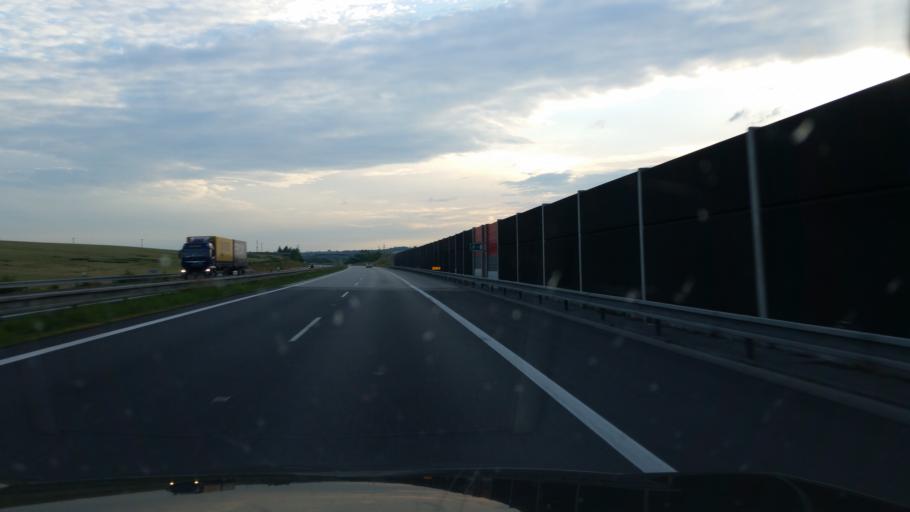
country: CZ
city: Studenka
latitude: 49.7414
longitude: 18.0602
